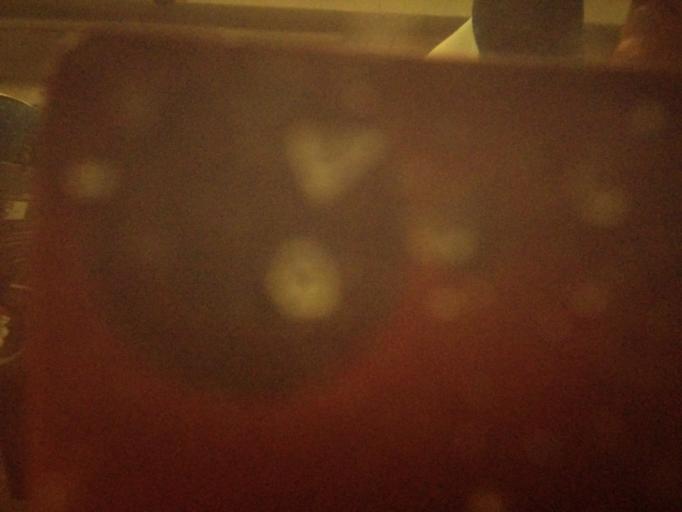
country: JP
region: Kanagawa
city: Yugawara
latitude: 35.1479
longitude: 139.1001
